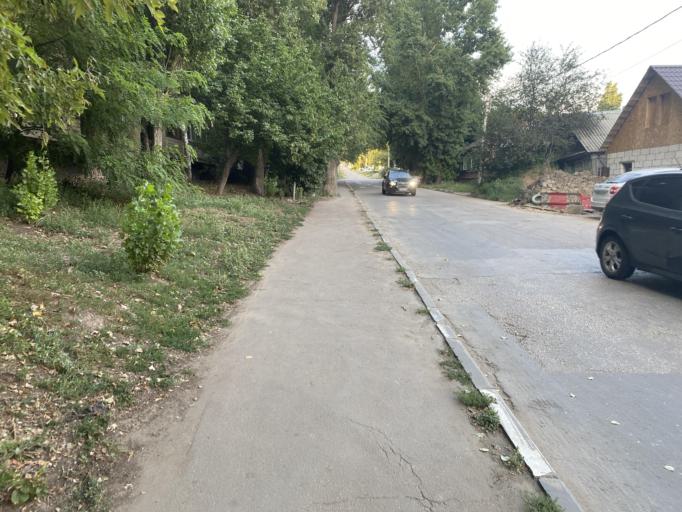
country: RU
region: Saratov
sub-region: Saratovskiy Rayon
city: Saratov
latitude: 51.5332
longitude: 46.0614
